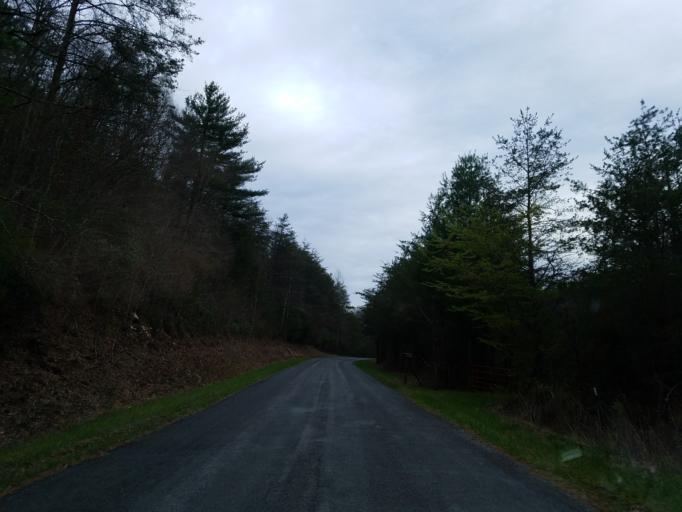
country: US
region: Georgia
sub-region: Fannin County
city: Blue Ridge
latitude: 34.7299
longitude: -84.2848
